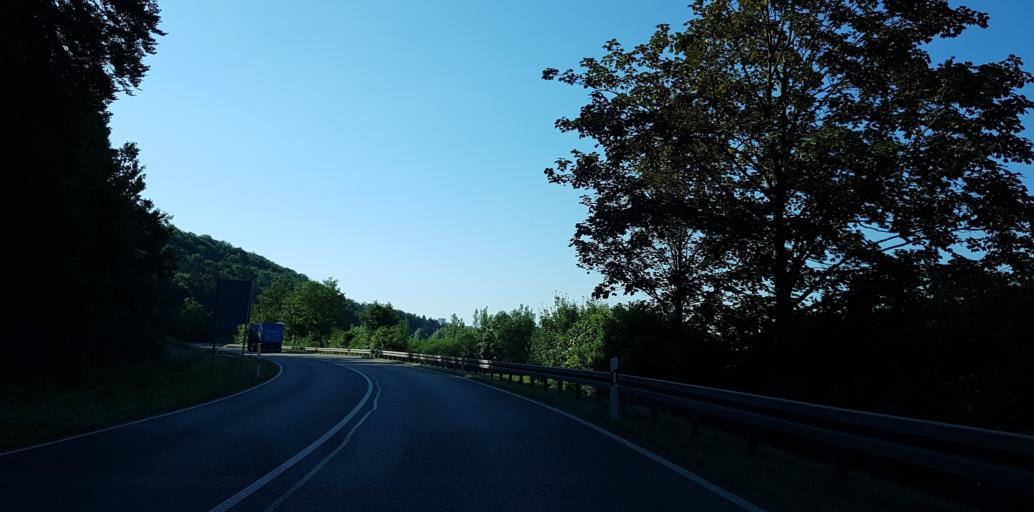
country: DE
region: Baden-Wuerttemberg
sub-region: Tuebingen Region
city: Allmendingen
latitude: 48.3480
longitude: 9.7148
